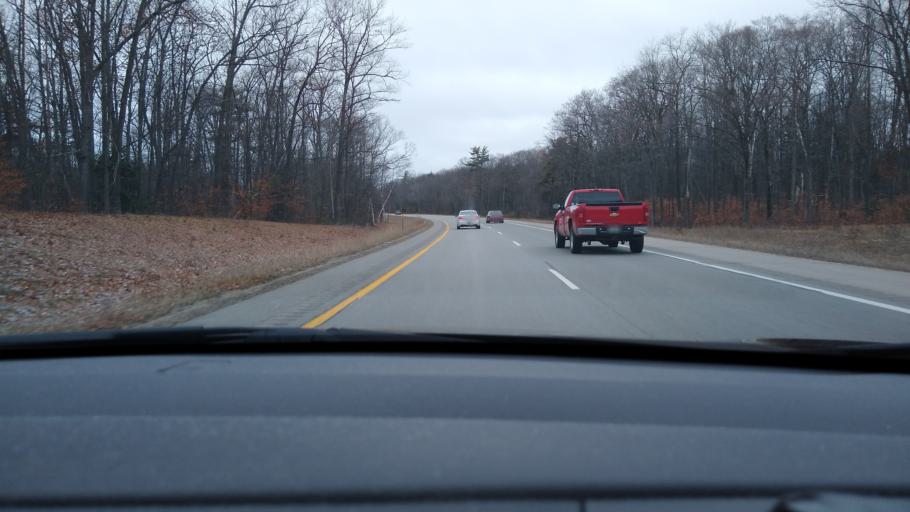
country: US
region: Michigan
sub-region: Otsego County
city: Gaylord
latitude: 44.9453
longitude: -84.6659
